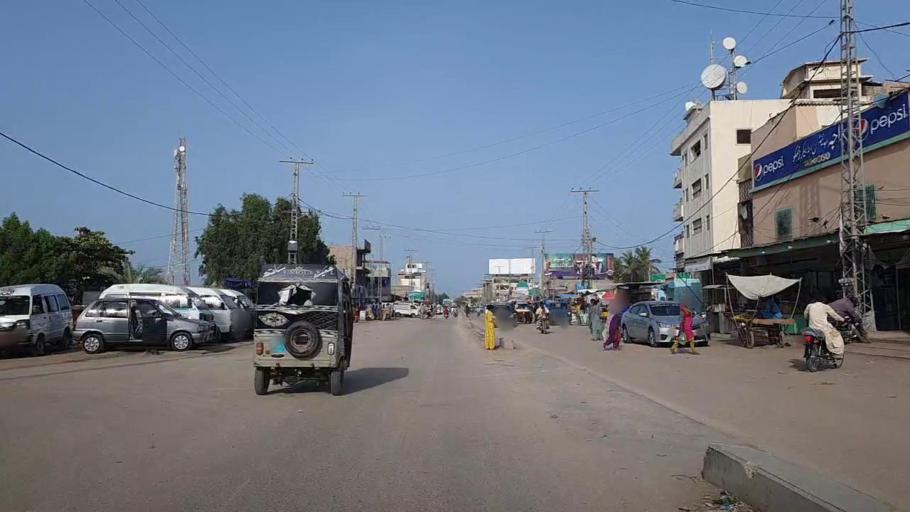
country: PK
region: Sindh
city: Thatta
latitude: 24.7512
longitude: 67.9204
